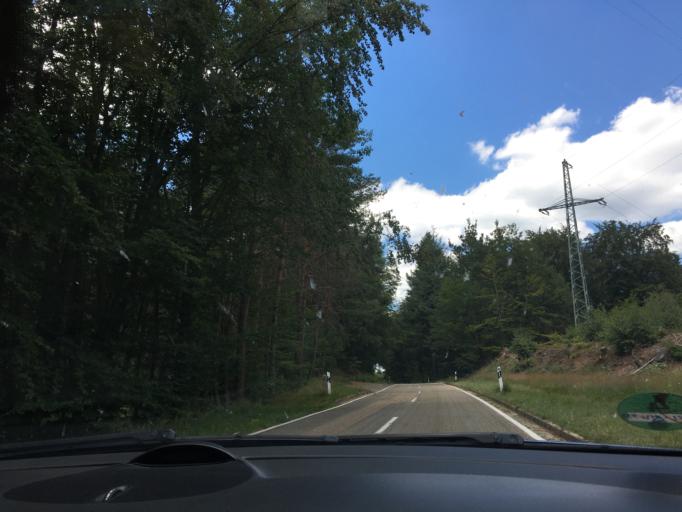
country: DE
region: Rheinland-Pfalz
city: Hauenstein
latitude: 49.2127
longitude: 7.8394
